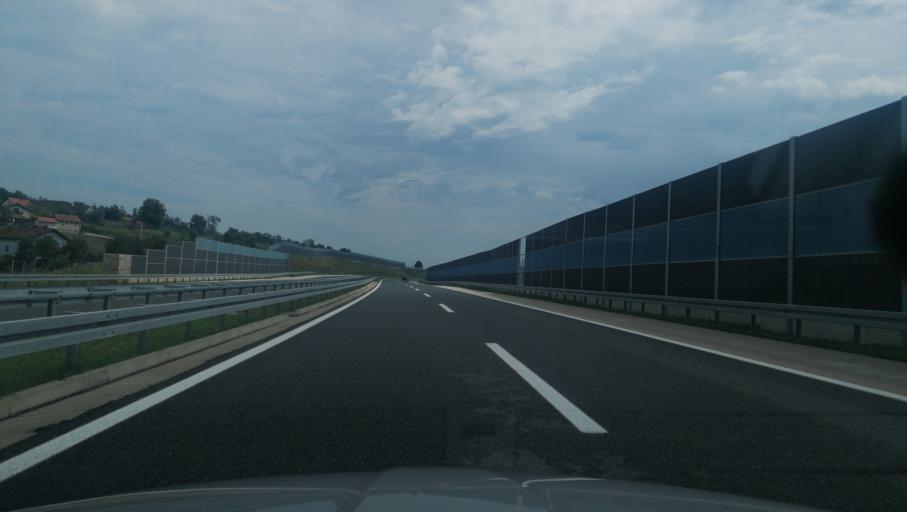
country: BA
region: Republika Srpska
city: Stanari
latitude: 44.8129
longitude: 17.8614
